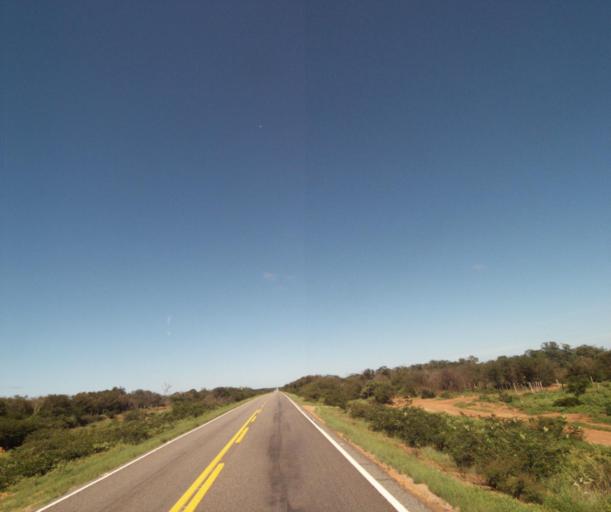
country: BR
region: Bahia
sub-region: Palmas De Monte Alto
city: Palmas de Monte Alto
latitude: -14.2515
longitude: -43.1876
